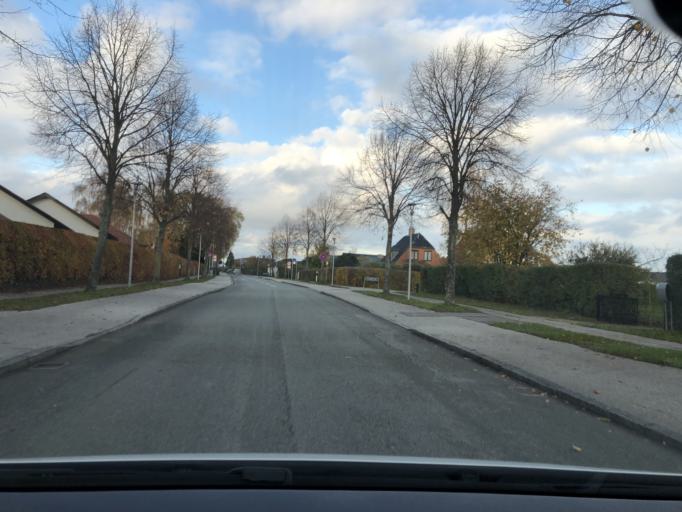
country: DK
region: Capital Region
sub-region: Tarnby Kommune
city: Tarnby
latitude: 55.6205
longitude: 12.5975
